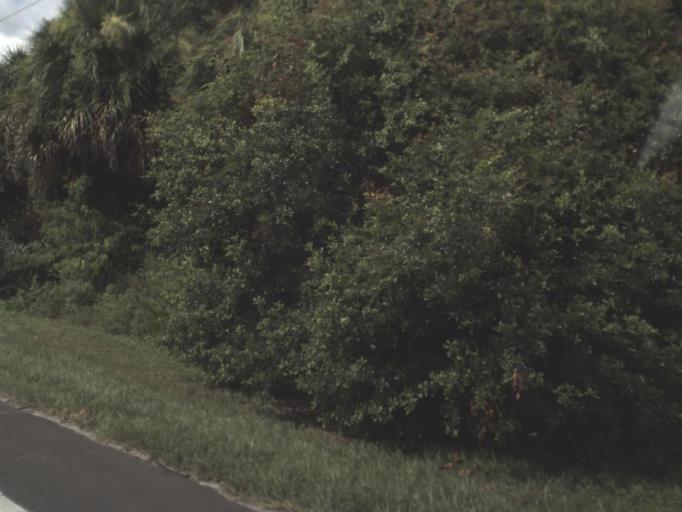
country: US
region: Florida
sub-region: Hillsborough County
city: Plant City
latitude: 28.0826
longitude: -82.1390
